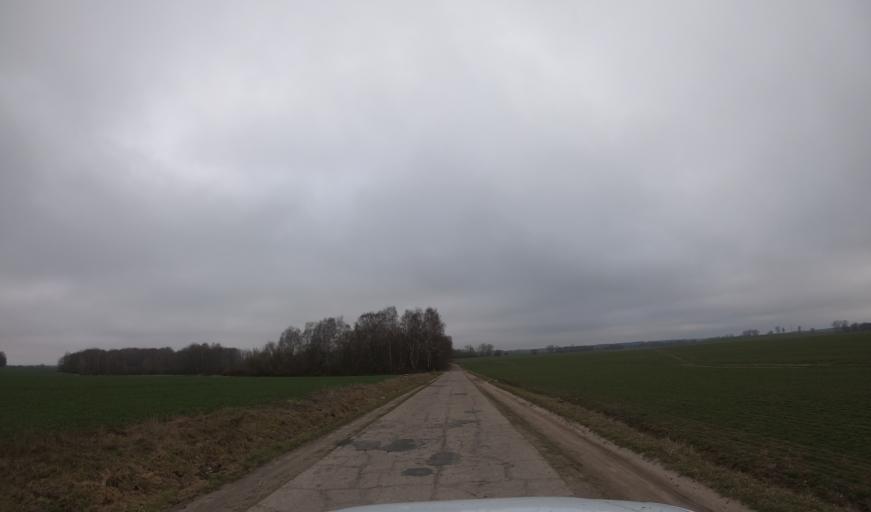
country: PL
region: West Pomeranian Voivodeship
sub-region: Powiat gryficki
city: Ploty
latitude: 53.8567
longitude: 15.2659
